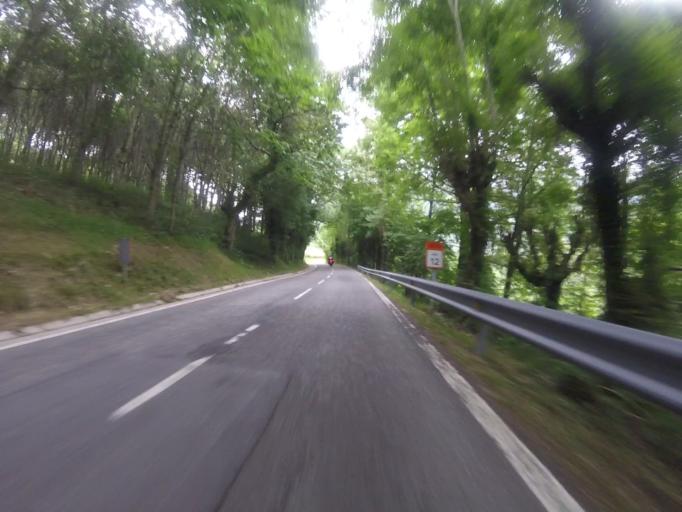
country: ES
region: Navarre
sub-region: Provincia de Navarra
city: Ezkurra
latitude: 43.0857
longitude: -1.8446
